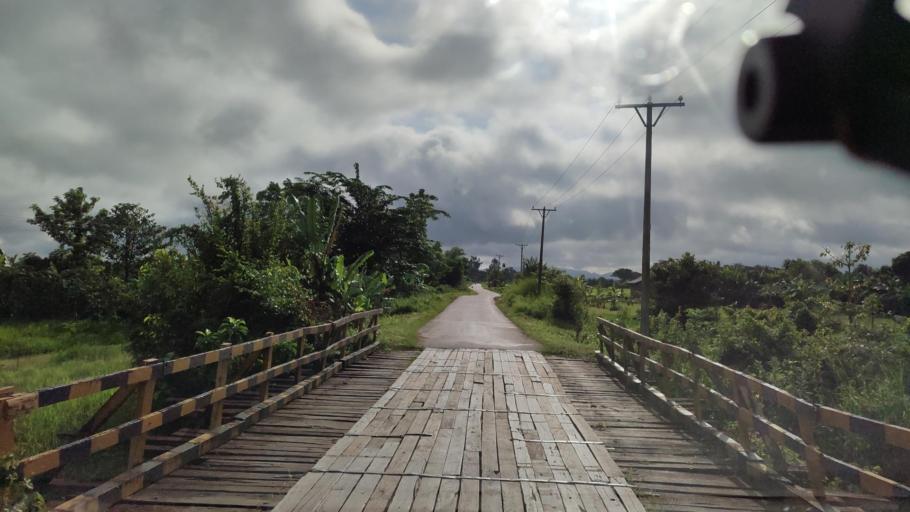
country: MM
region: Bago
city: Letpandan
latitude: 17.7932
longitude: 95.8051
